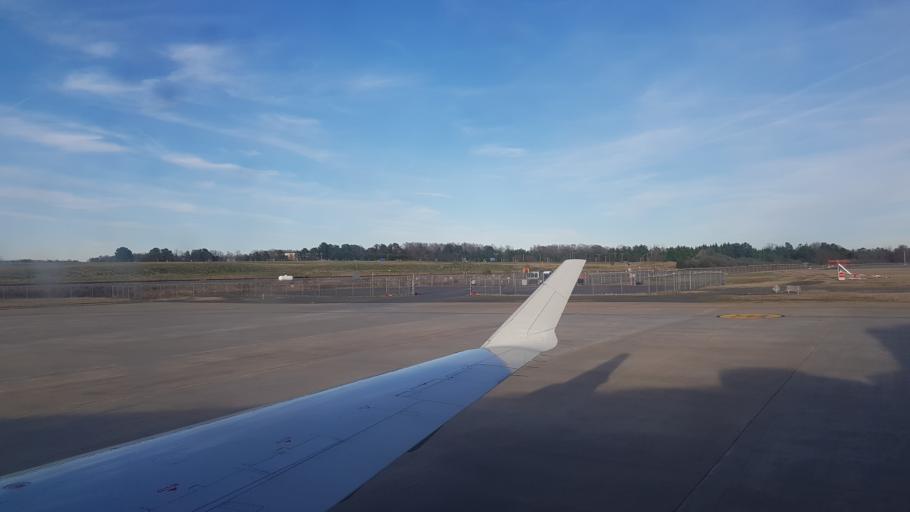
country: US
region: North Carolina
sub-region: Mecklenburg County
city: Charlotte
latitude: 35.2257
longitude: -80.9384
